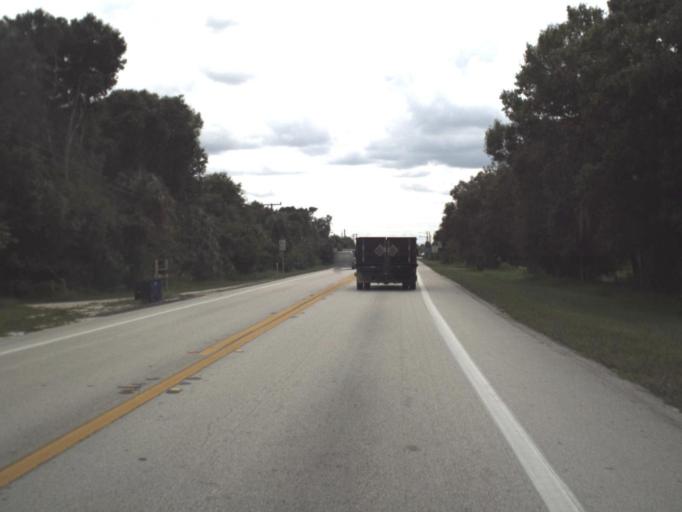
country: US
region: Florida
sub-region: Lee County
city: Fort Myers Shores
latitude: 26.7057
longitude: -81.7603
